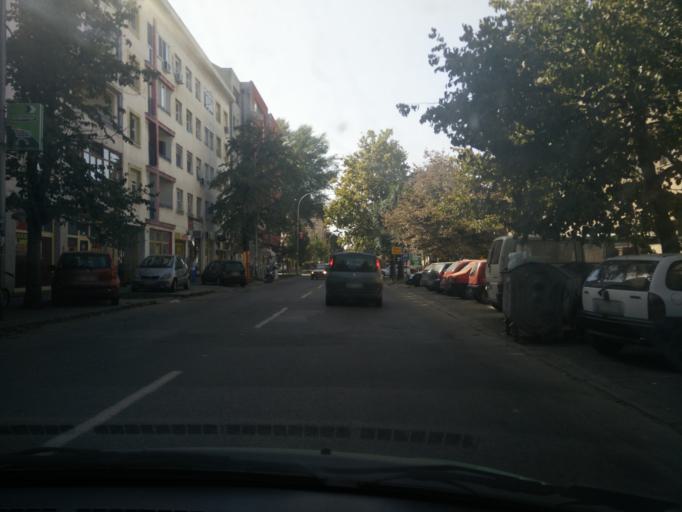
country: RS
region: Autonomna Pokrajina Vojvodina
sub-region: Juznobacki Okrug
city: Novi Sad
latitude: 45.2616
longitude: 19.8526
